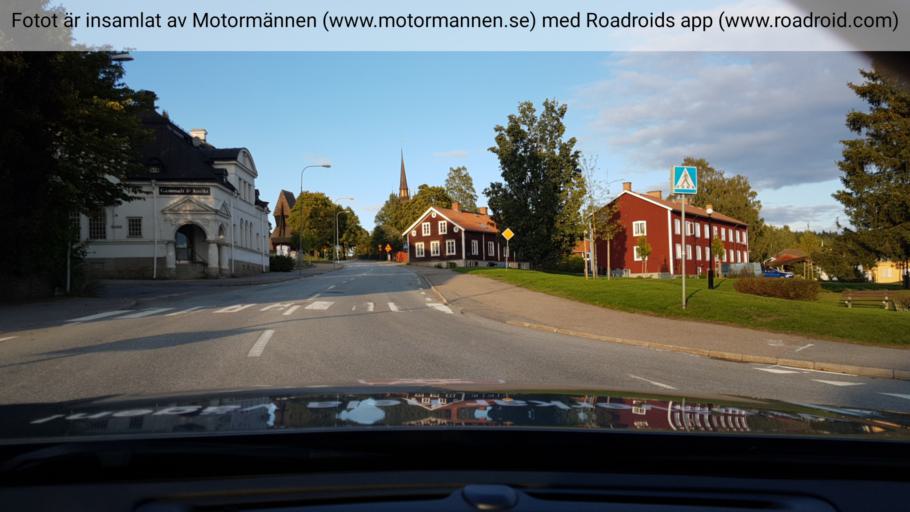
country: SE
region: OErebro
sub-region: Ljusnarsbergs Kommun
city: Kopparberg
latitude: 59.8762
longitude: 14.9943
